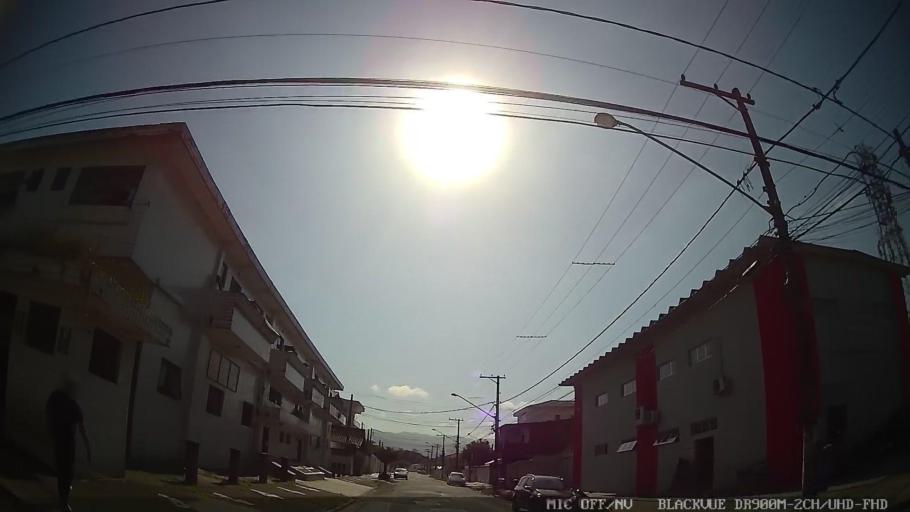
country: BR
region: Sao Paulo
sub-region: Santos
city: Santos
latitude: -23.9414
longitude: -46.3008
